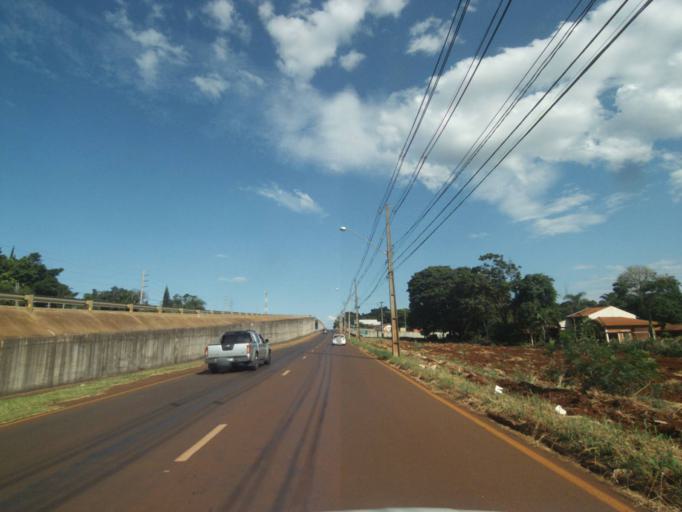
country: BR
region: Parana
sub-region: Londrina
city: Londrina
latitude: -23.3464
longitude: -51.1746
